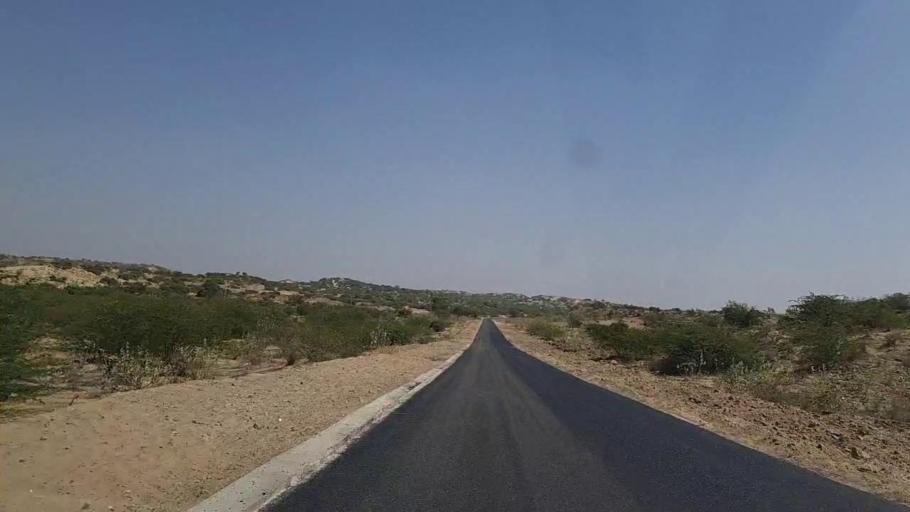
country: PK
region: Sindh
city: Diplo
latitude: 24.4802
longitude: 69.5181
